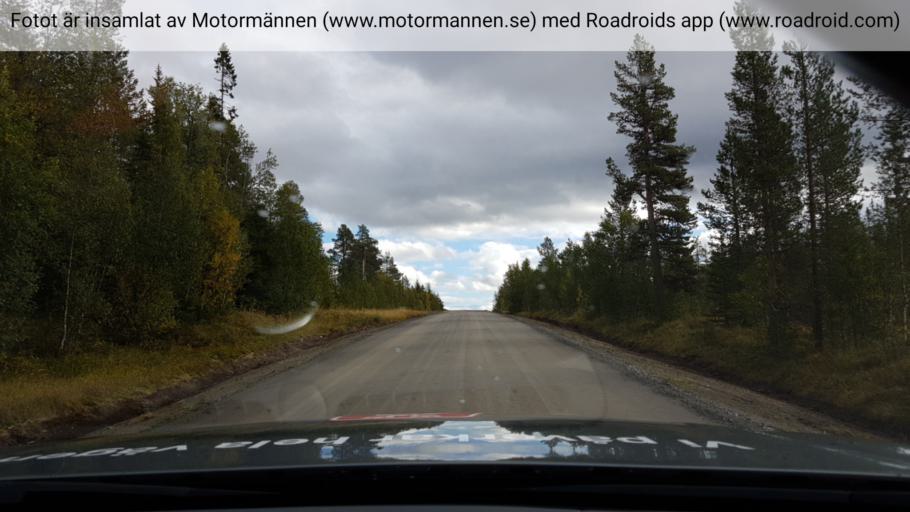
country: NO
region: Nord-Trondelag
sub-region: Snasa
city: Snaase
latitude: 63.7262
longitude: 12.5879
